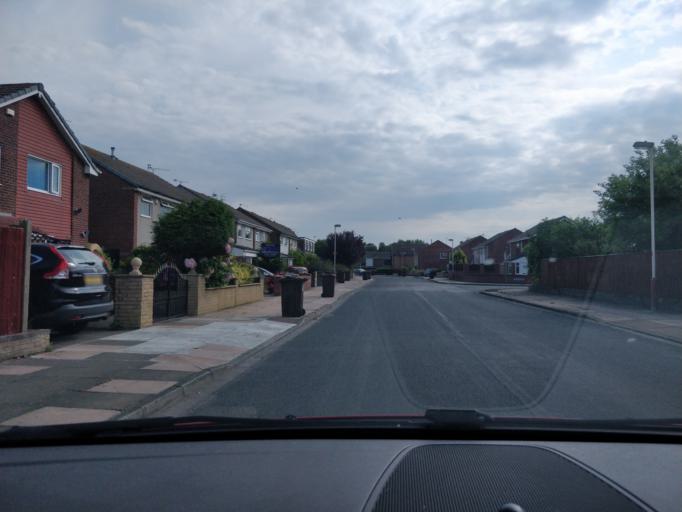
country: GB
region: England
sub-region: Lancashire
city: Banks
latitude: 53.6759
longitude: -2.9626
